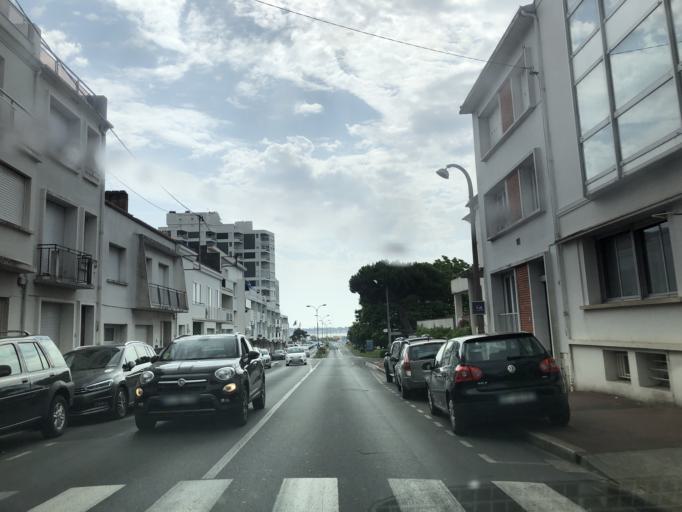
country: FR
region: Poitou-Charentes
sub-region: Departement de la Charente-Maritime
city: Royan
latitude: 45.6207
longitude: -1.0362
